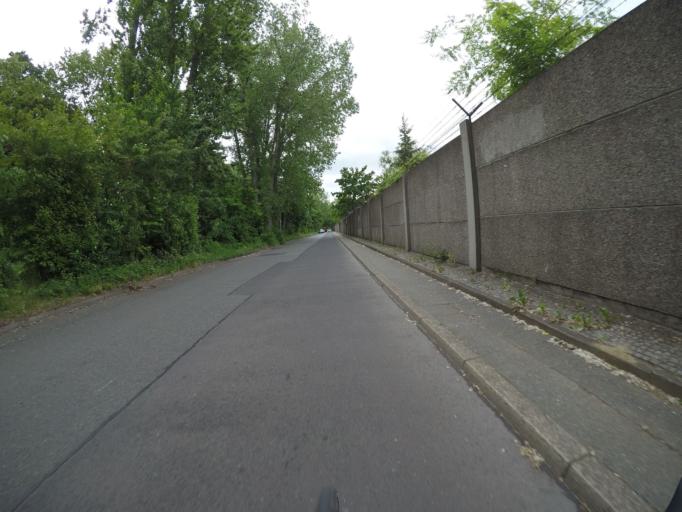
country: DE
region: Berlin
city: Reinickendorf
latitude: 52.5555
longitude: 13.3249
